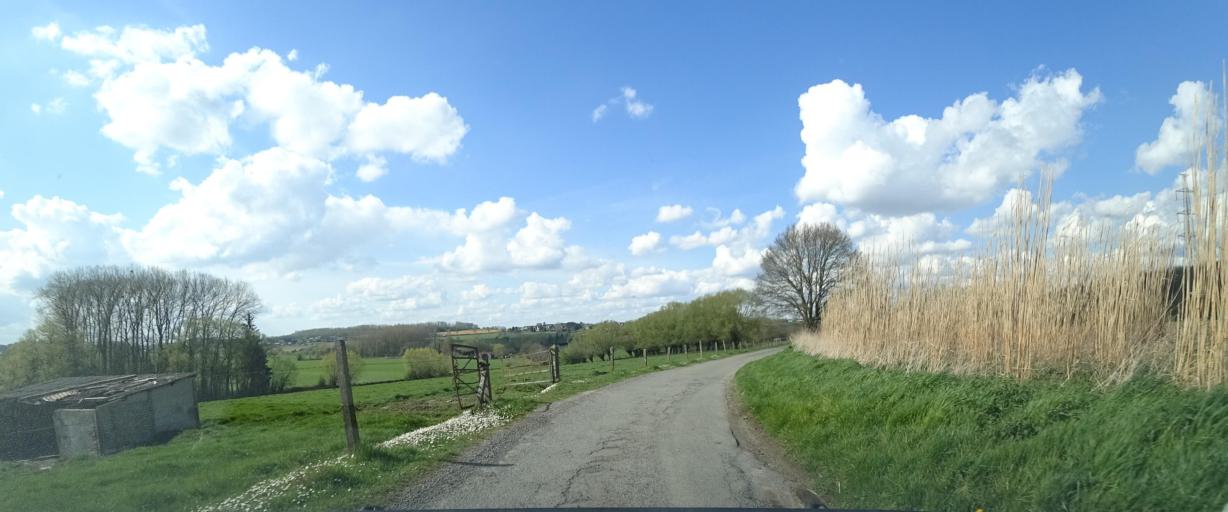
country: BE
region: Wallonia
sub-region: Province du Brabant Wallon
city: Tubize
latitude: 50.6591
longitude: 4.1955
